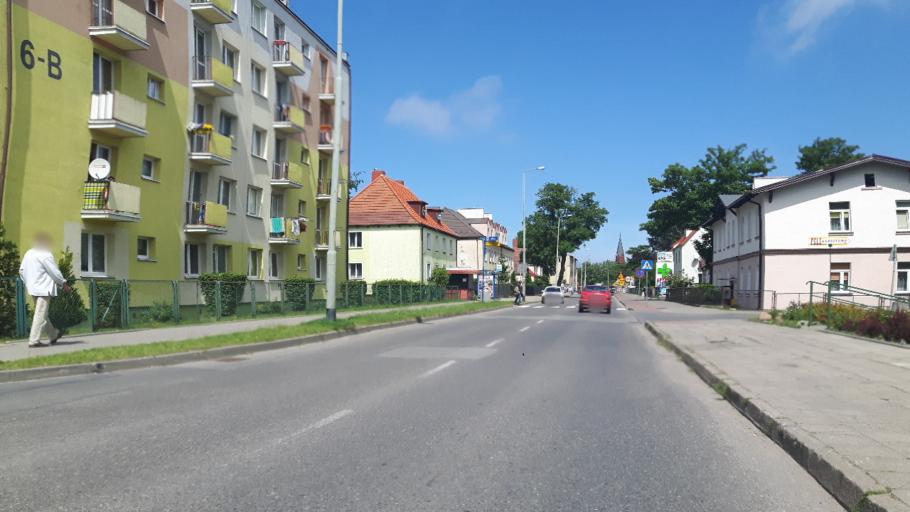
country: PL
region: Pomeranian Voivodeship
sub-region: Powiat slupski
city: Ustka
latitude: 54.5777
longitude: 16.8545
